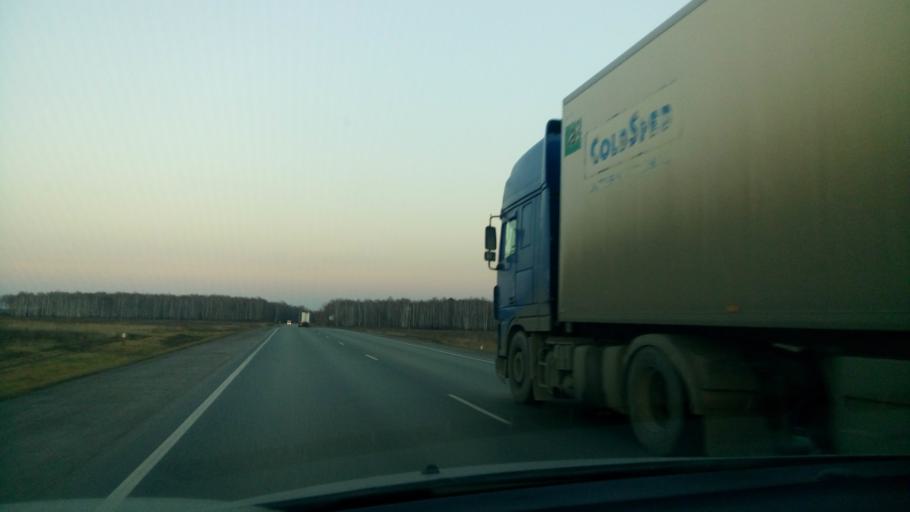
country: RU
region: Sverdlovsk
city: Pyshma
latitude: 56.9246
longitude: 63.1470
